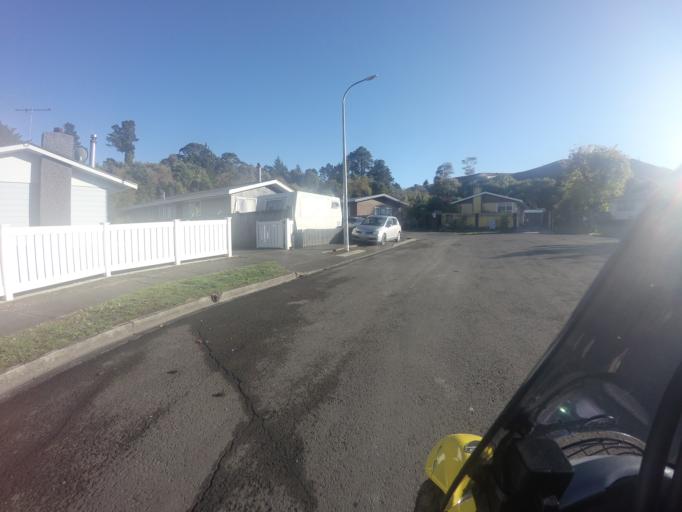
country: NZ
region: Gisborne
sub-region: Gisborne District
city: Gisborne
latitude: -38.6663
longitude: 178.0575
